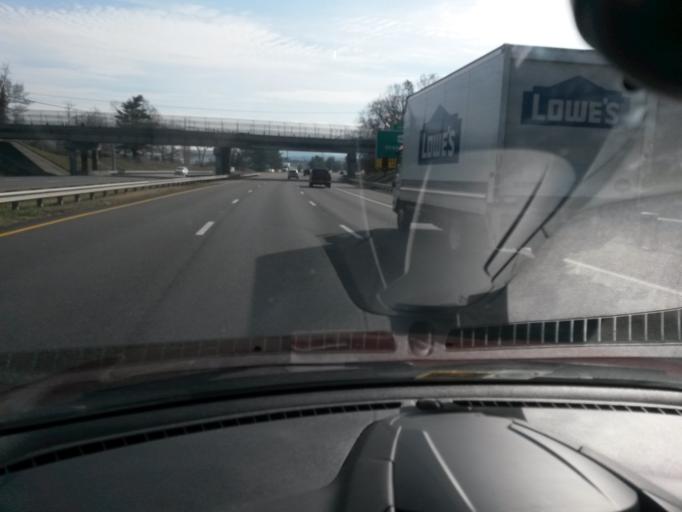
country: US
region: Virginia
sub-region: City of Roanoke
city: Roanoke
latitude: 37.2910
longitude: -79.9423
